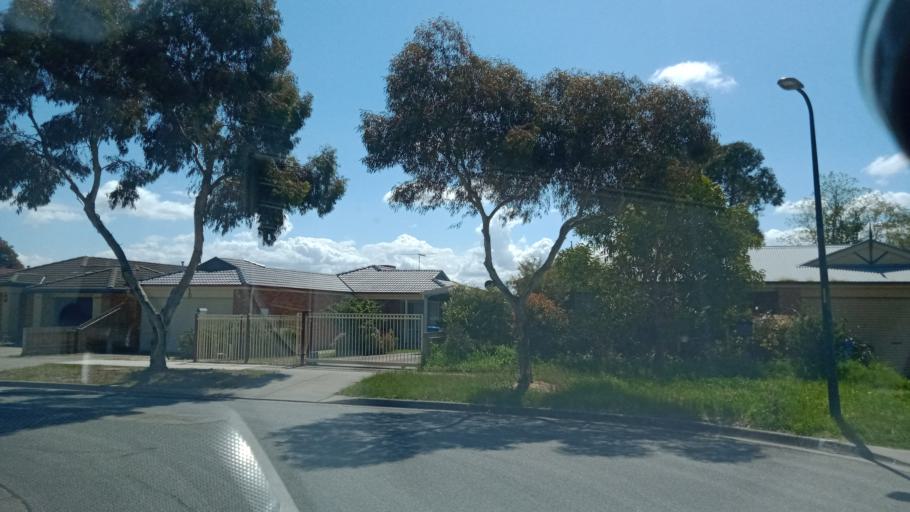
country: AU
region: Victoria
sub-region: Casey
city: Cranbourne West
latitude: -38.0939
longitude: 145.2615
